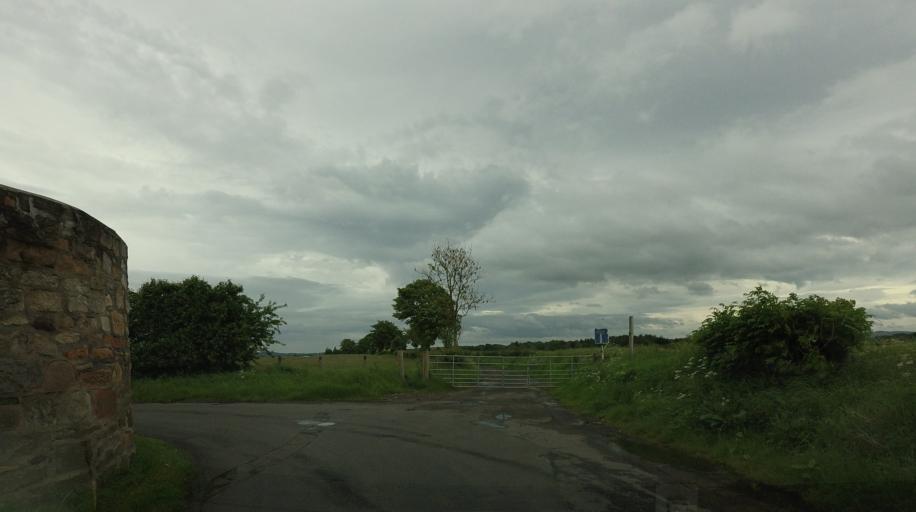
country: GB
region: Scotland
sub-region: West Lothian
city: Broxburn
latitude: 55.9215
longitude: -3.4443
